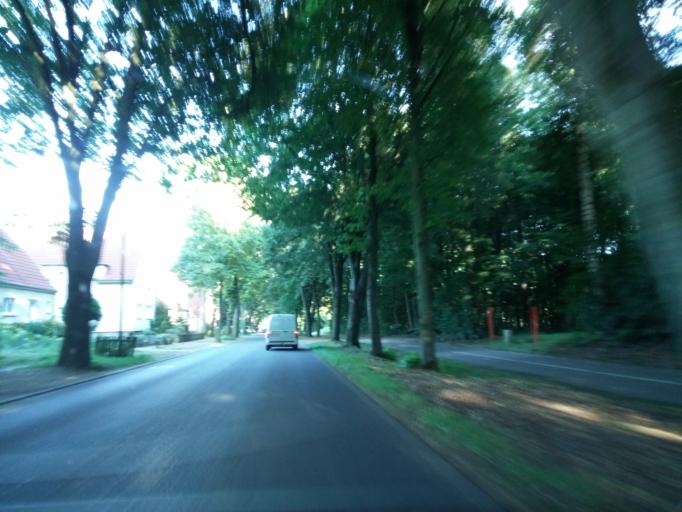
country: DE
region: North Rhine-Westphalia
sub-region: Regierungsbezirk Munster
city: Gladbeck
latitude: 51.6086
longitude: 7.0011
